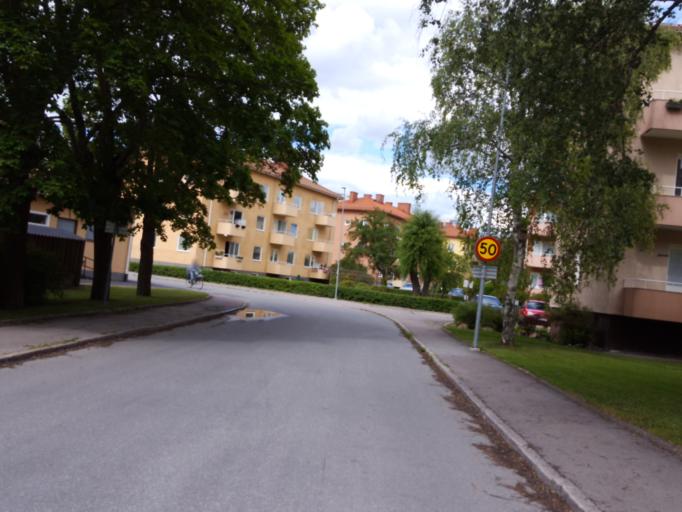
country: SE
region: Uppsala
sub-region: Uppsala Kommun
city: Uppsala
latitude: 59.8467
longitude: 17.6343
